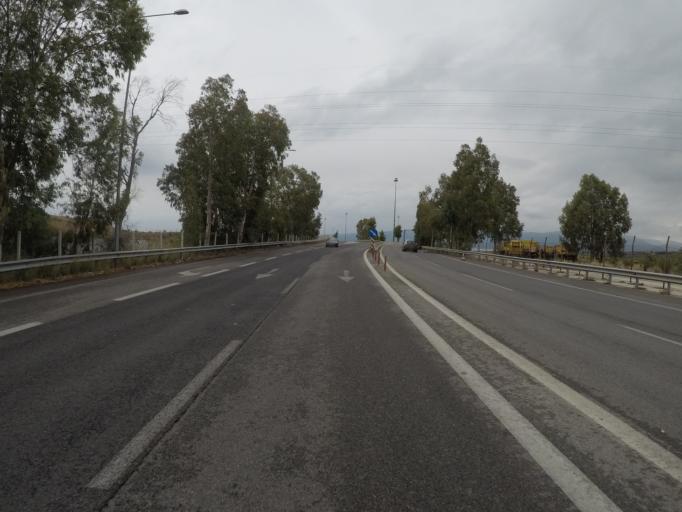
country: GR
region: Peloponnese
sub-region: Nomos Korinthias
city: Isthmia
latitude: 37.9267
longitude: 22.9980
